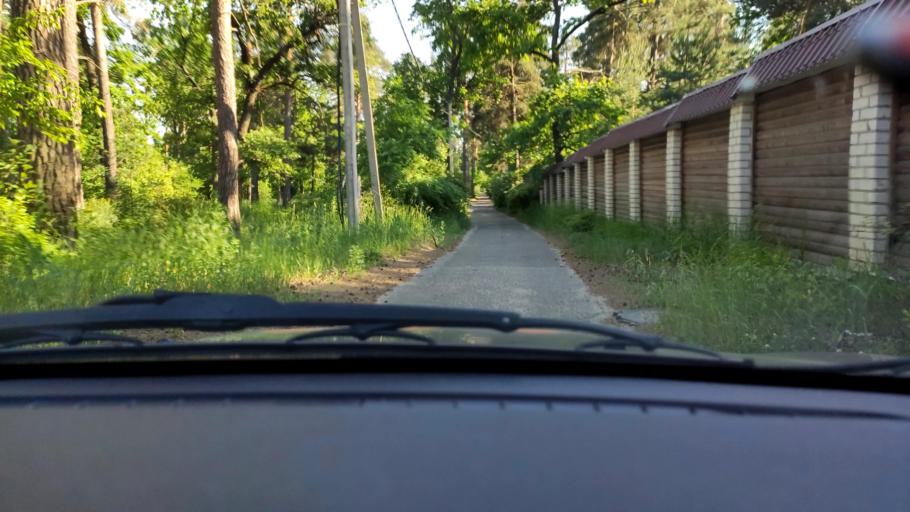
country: RU
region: Voronezj
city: Somovo
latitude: 51.7517
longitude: 39.3744
